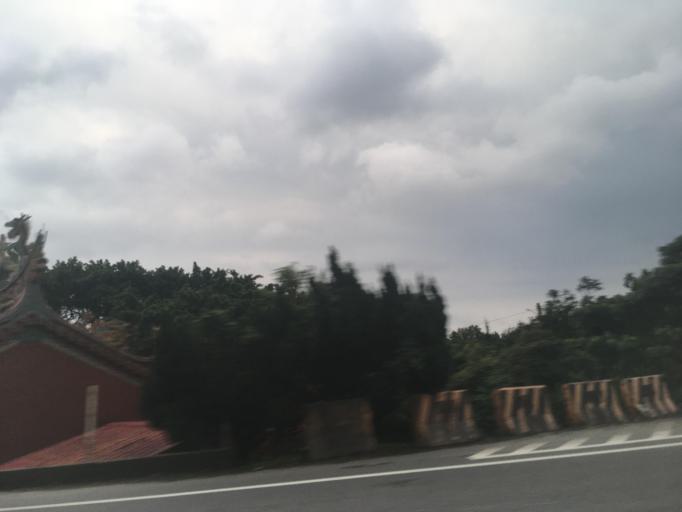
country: TW
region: Taiwan
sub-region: Yilan
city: Yilan
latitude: 24.9337
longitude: 121.8846
